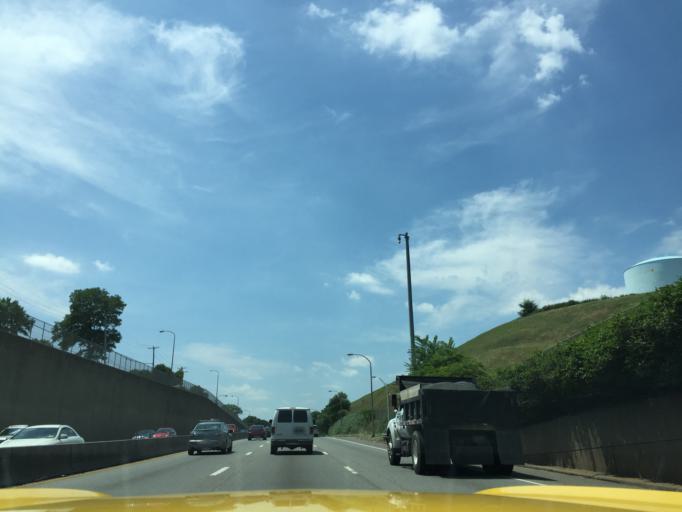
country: US
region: Pennsylvania
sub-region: Montgomery County
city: Bala-Cynwyd
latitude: 40.0143
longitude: -75.1787
